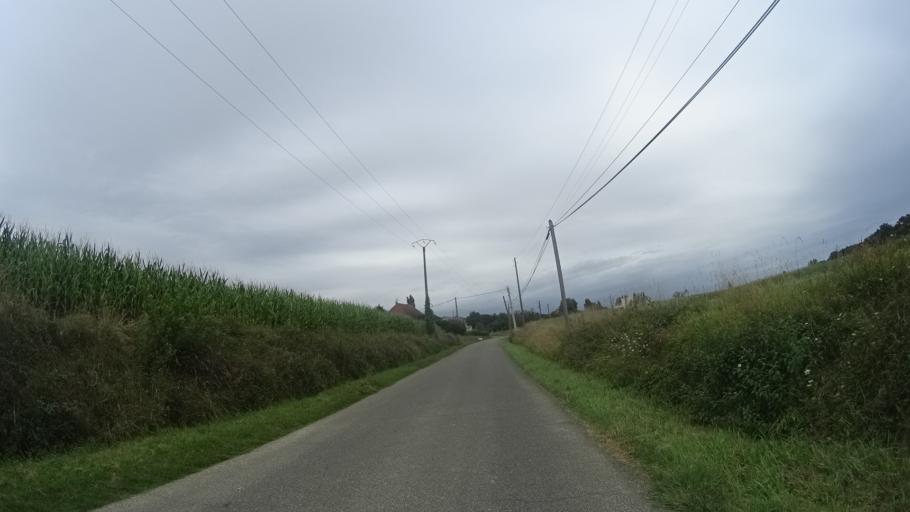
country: FR
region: Aquitaine
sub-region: Departement des Pyrenees-Atlantiques
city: Orthez
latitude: 43.4792
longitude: -0.7250
